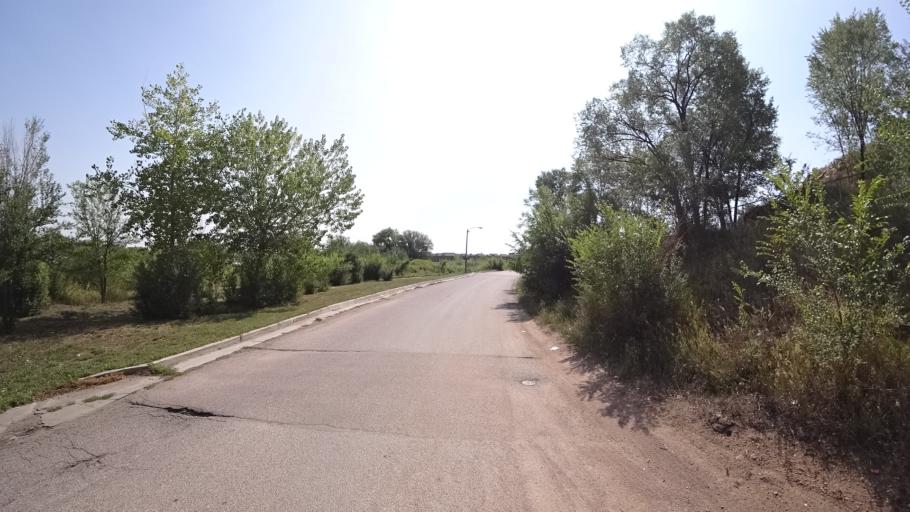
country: US
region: Colorado
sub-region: El Paso County
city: Colorado Springs
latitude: 38.8319
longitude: -104.8445
